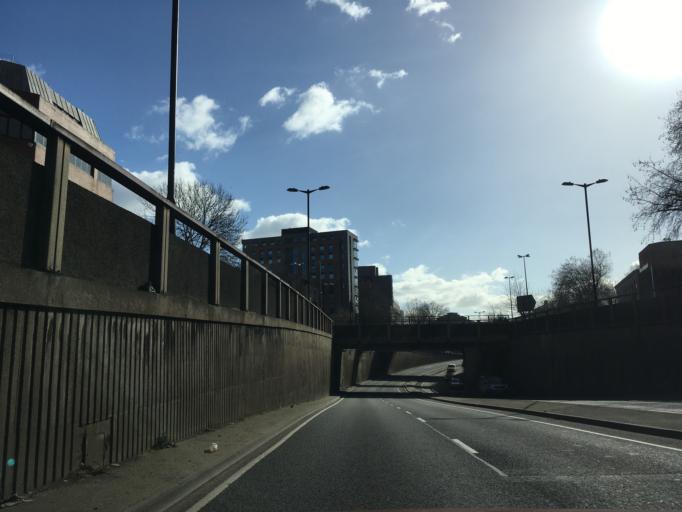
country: GB
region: England
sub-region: Bristol
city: Bristol
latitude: 51.4566
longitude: -2.5842
